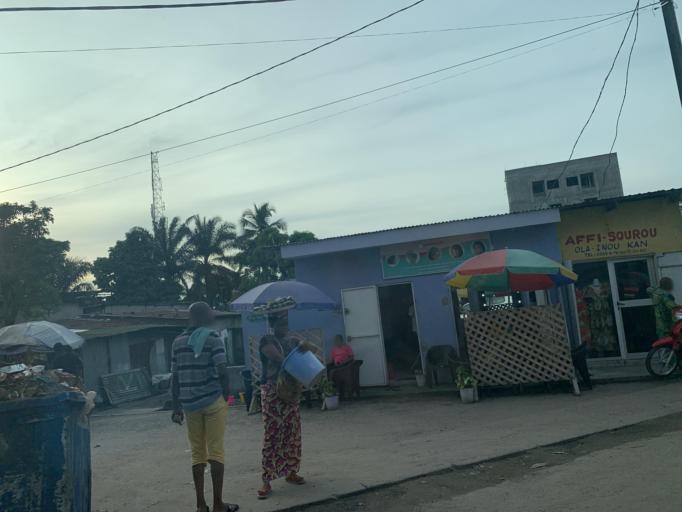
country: CG
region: Brazzaville
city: Brazzaville
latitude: -4.2601
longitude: 15.2898
